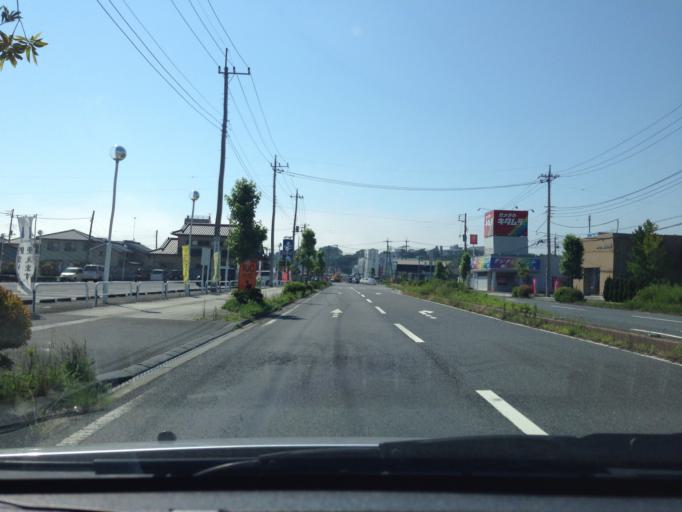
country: JP
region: Ibaraki
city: Oarai
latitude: 36.3476
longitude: 140.5815
